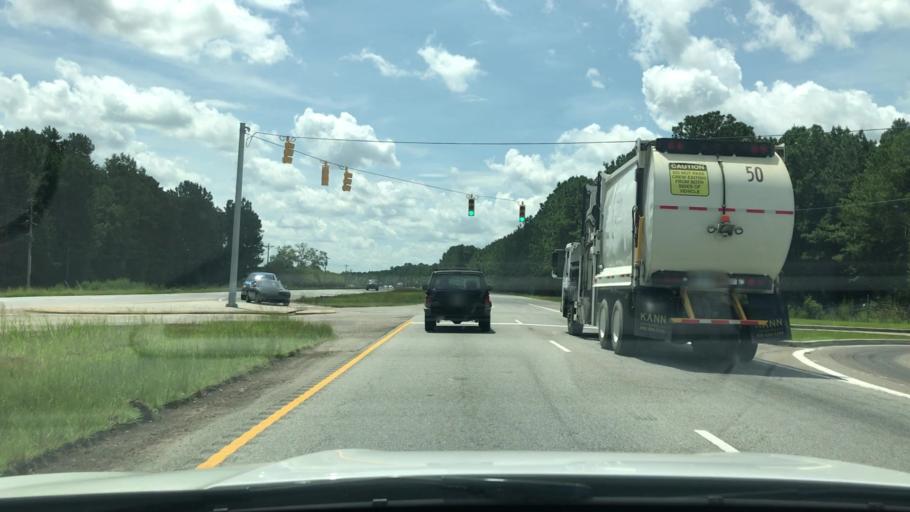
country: US
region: South Carolina
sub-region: Berkeley County
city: Goose Creek
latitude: 33.0643
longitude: -80.0350
